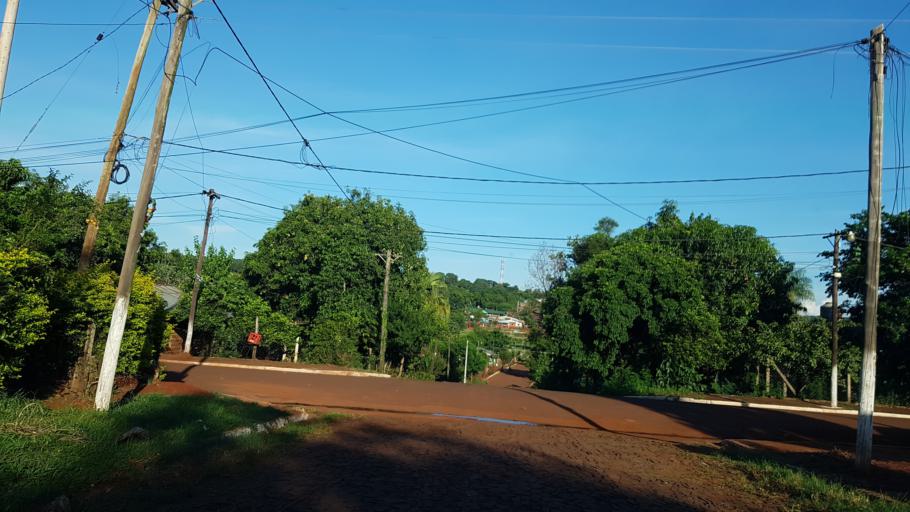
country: AR
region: Misiones
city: Puerto Libertad
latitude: -25.9171
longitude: -54.5880
